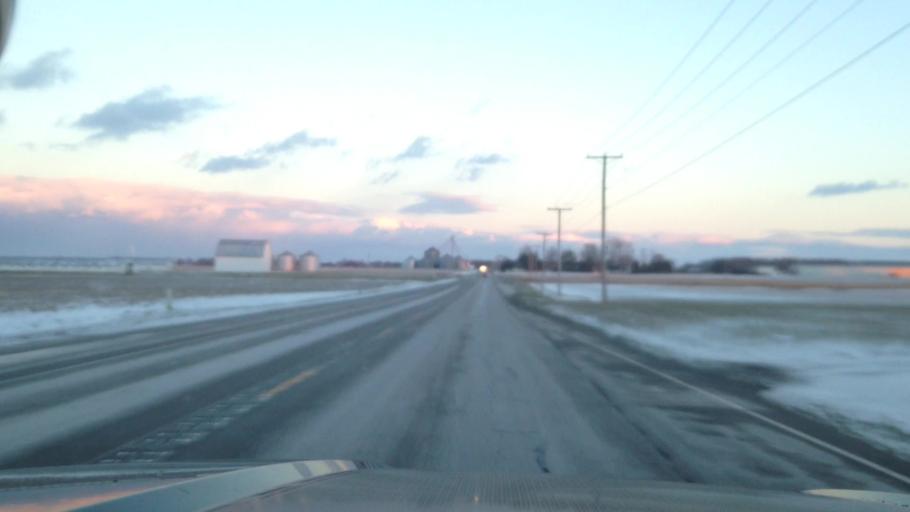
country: US
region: Indiana
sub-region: Randolph County
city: Union City
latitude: 40.1785
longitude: -84.8620
